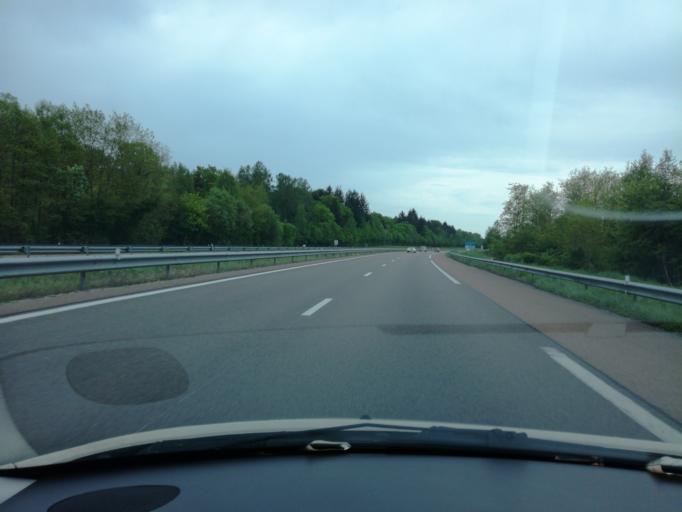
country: FR
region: Franche-Comte
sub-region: Departement du Jura
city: Mont-sous-Vaudrey
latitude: 46.9396
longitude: 5.5543
